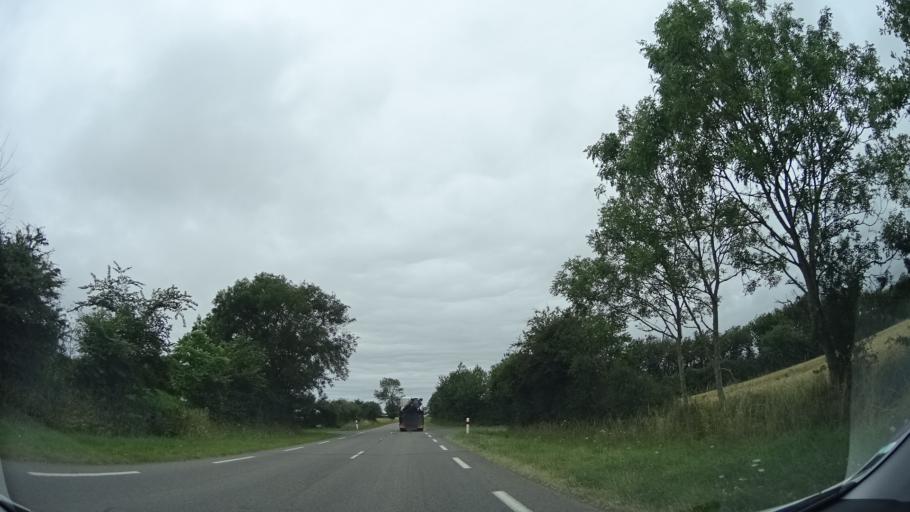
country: FR
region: Lower Normandy
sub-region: Departement de la Manche
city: Portbail
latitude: 49.3636
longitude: -1.7070
